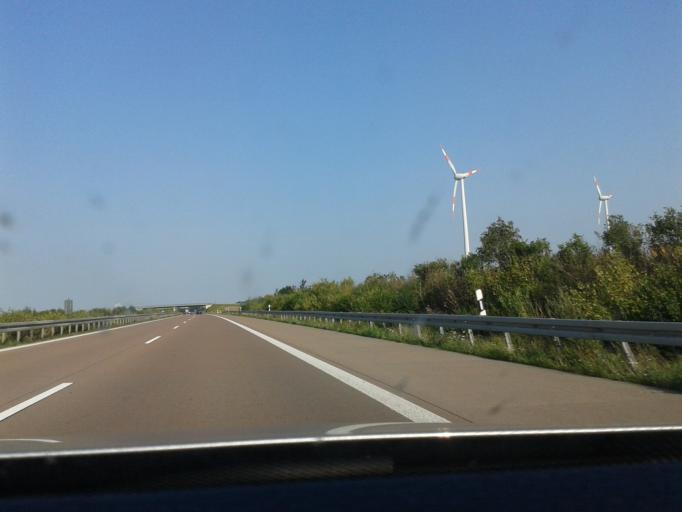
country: DE
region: Saxony-Anhalt
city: Schafstadt
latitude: 51.4001
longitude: 11.7255
